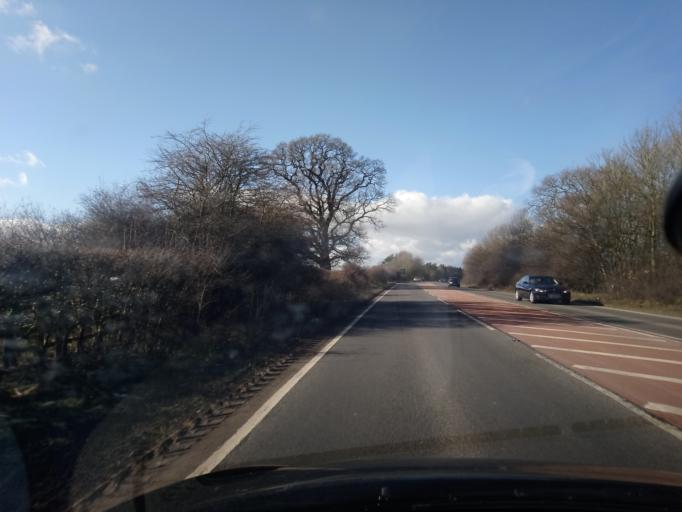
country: GB
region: England
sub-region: Shropshire
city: Whitchurch
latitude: 52.9567
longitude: -2.6884
